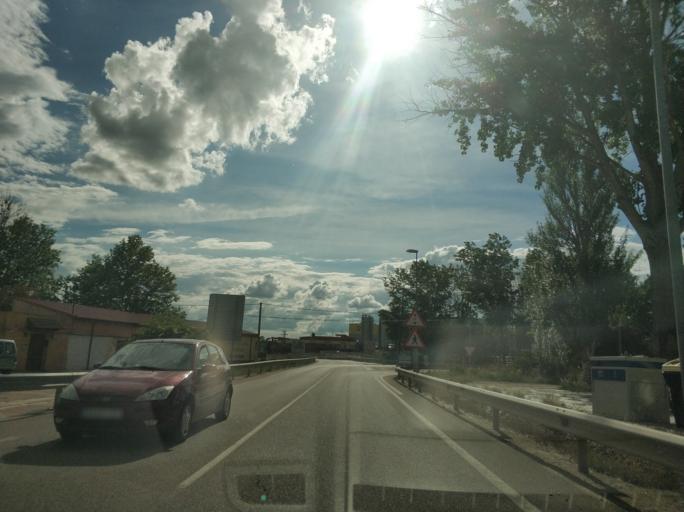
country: ES
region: Castille and Leon
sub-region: Provincia de Burgos
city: Aranda de Duero
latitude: 41.6762
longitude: -3.6961
